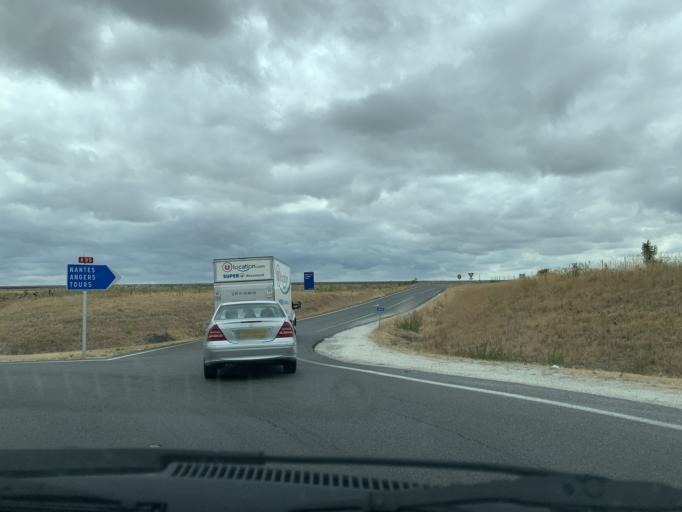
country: FR
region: Centre
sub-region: Departement d'Indre-et-Loire
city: Athee-sur-Cher
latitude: 47.3025
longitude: 0.8875
